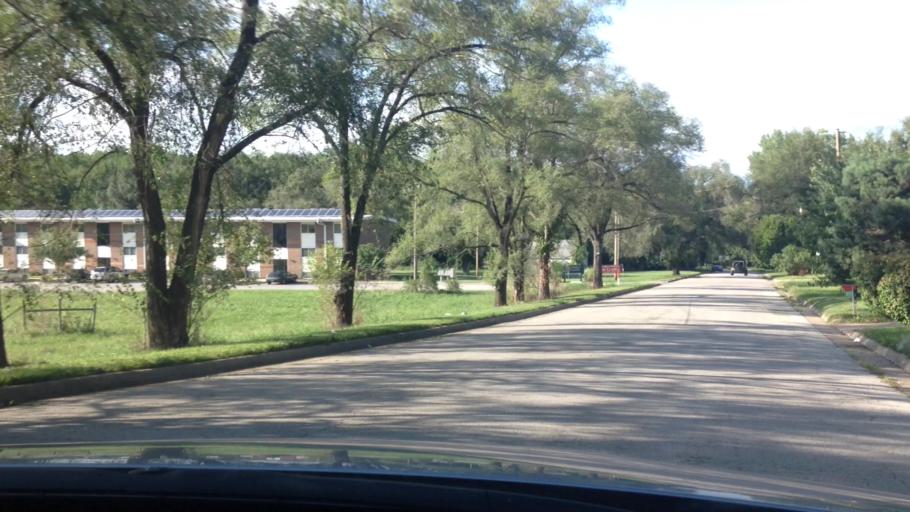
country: US
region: Kansas
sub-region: Leavenworth County
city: Leavenworth
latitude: 39.2897
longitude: -94.9090
